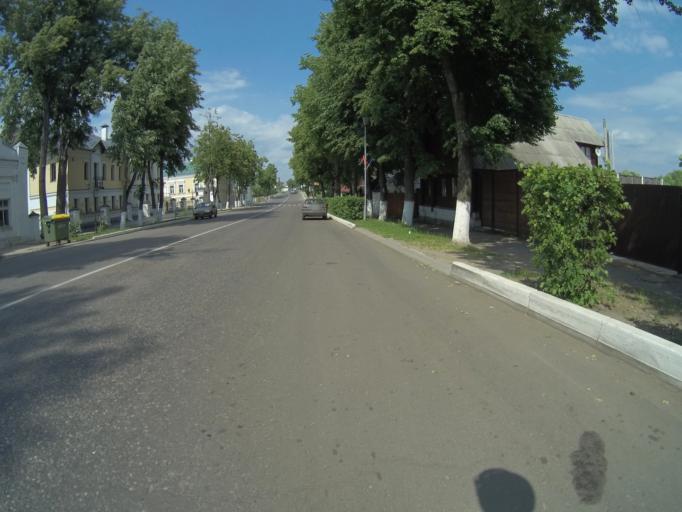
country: RU
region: Vladimir
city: Suzdal'
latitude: 56.4121
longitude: 40.4474
